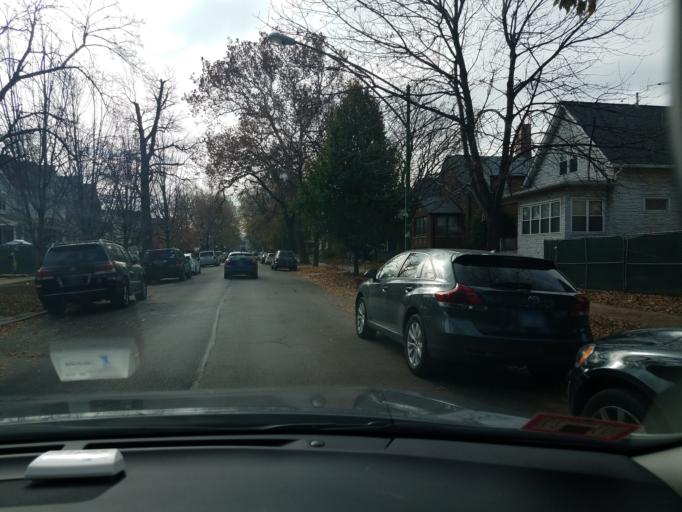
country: US
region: Illinois
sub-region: Cook County
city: Lincolnwood
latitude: 41.9492
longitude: -87.7339
